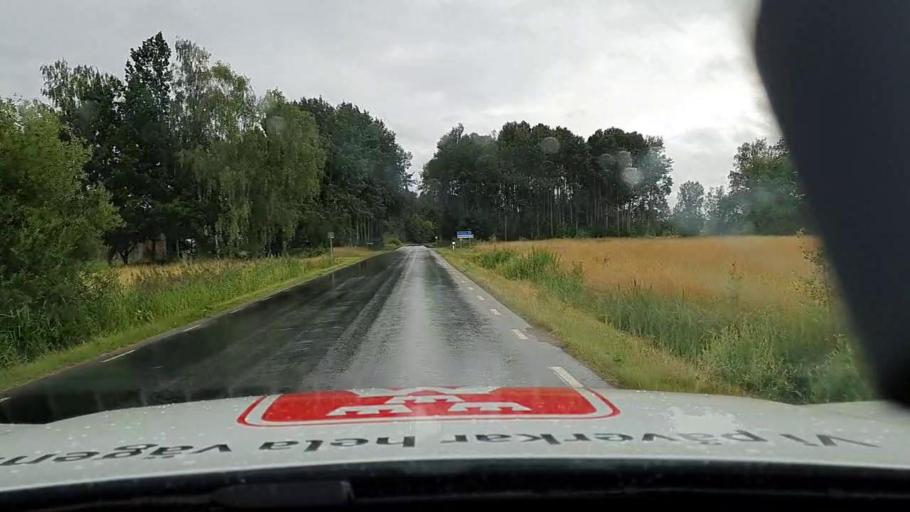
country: SE
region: Vaestra Goetaland
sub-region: Skovde Kommun
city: Stopen
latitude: 58.5623
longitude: 13.9831
